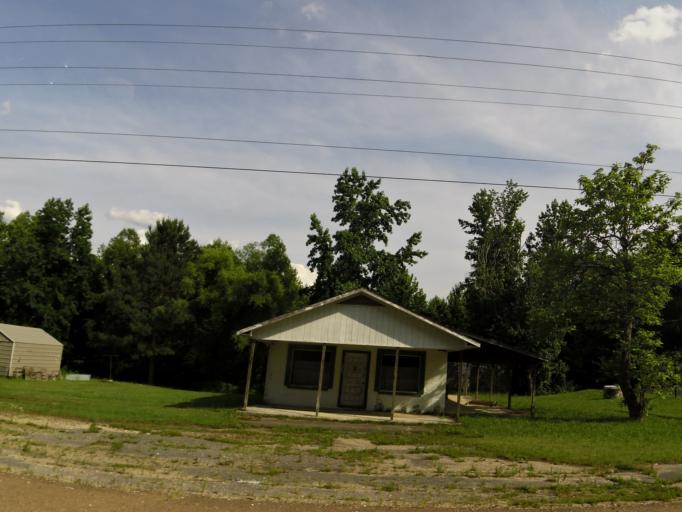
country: US
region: Tennessee
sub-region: Carroll County
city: Bruceton
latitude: 36.0367
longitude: -88.1910
